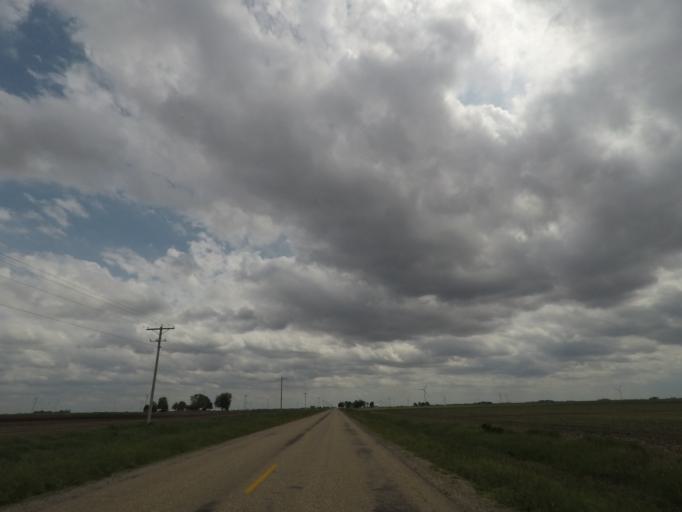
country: US
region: Illinois
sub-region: Macon County
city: Maroa
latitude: 40.0662
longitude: -89.0860
